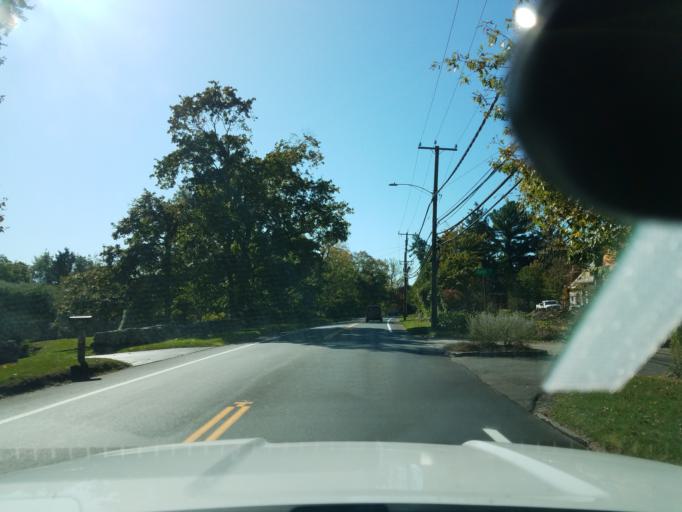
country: US
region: Connecticut
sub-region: Fairfield County
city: Cos Cob
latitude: 41.0545
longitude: -73.6166
